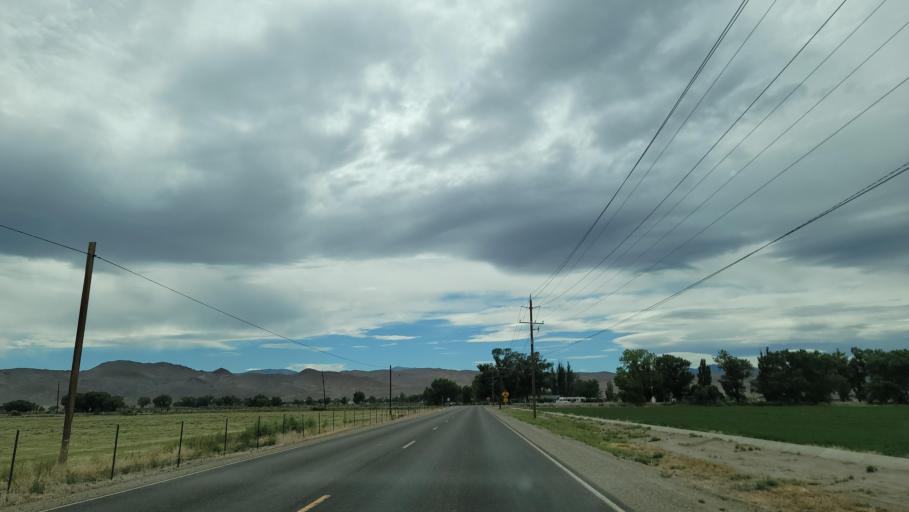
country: US
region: Nevada
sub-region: Lyon County
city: Yerington
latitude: 39.0481
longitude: -119.1782
